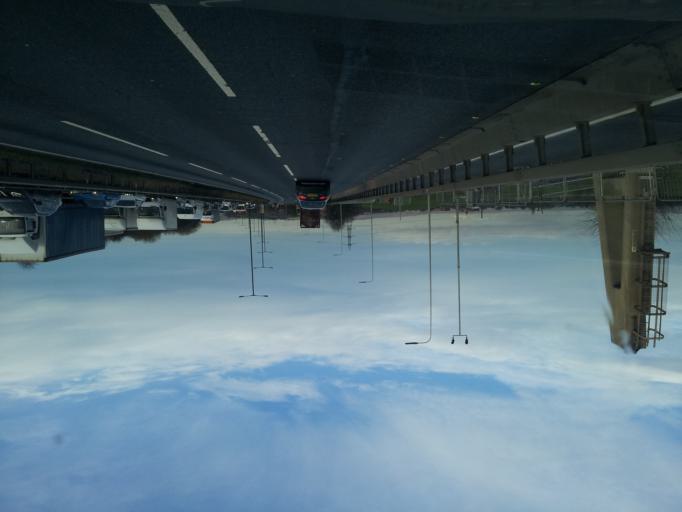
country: GB
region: England
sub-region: Manchester
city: Heywood
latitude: 53.5816
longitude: -2.1963
